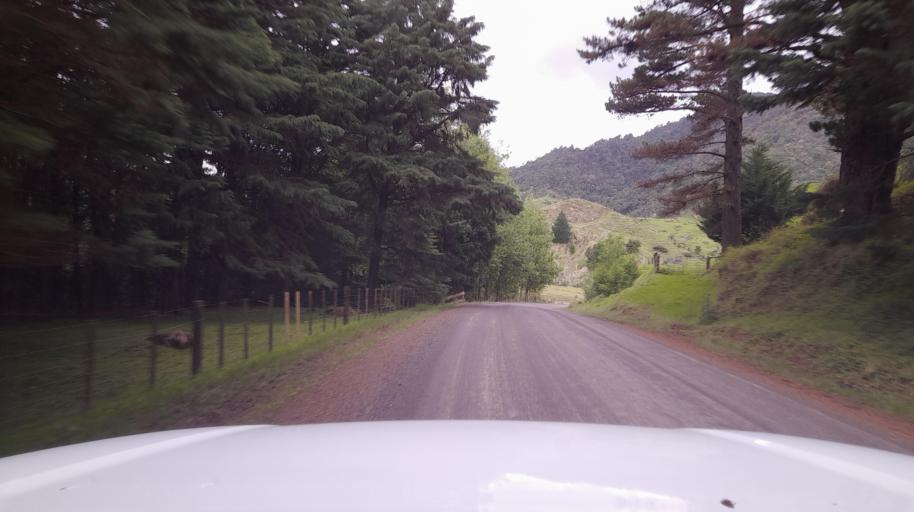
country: NZ
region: Northland
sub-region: Far North District
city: Kaitaia
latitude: -35.3347
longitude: 173.3547
